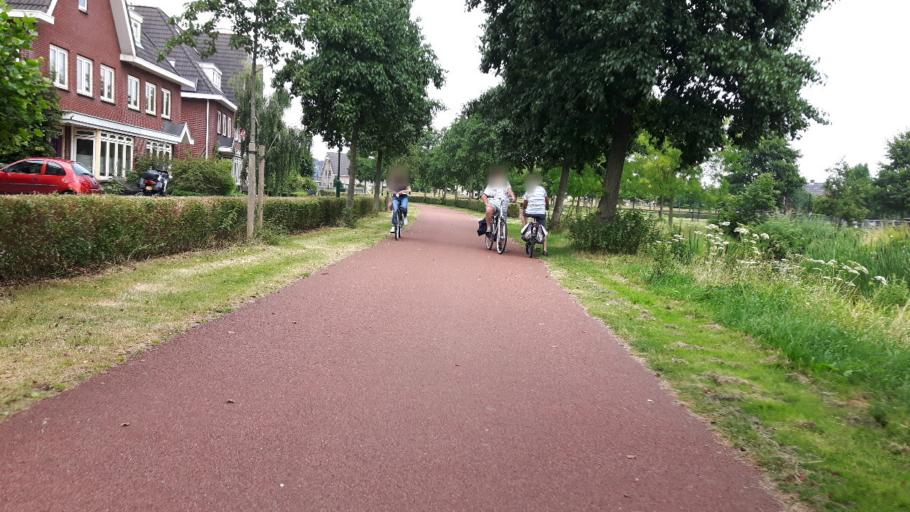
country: NL
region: Utrecht
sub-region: Gemeente Houten
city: Houten
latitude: 52.0205
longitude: 5.1832
